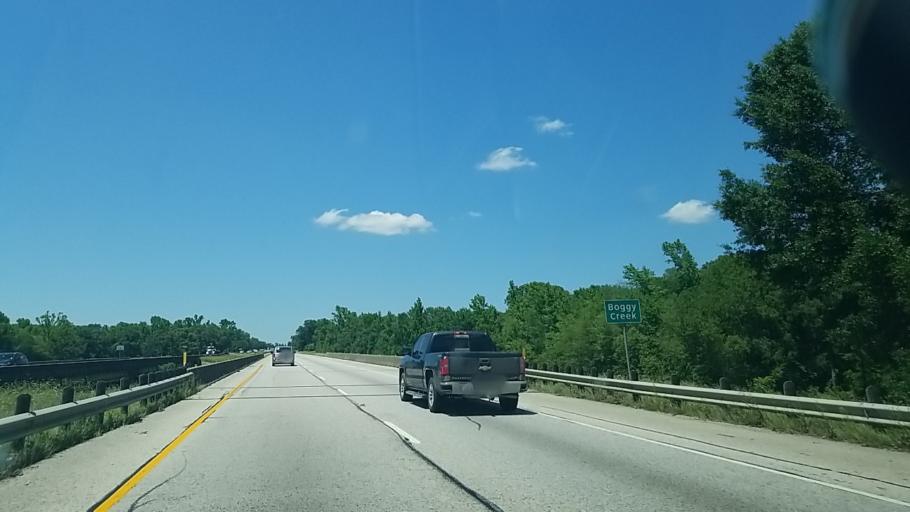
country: US
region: Texas
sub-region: Leon County
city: Centerville
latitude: 31.1882
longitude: -95.9918
